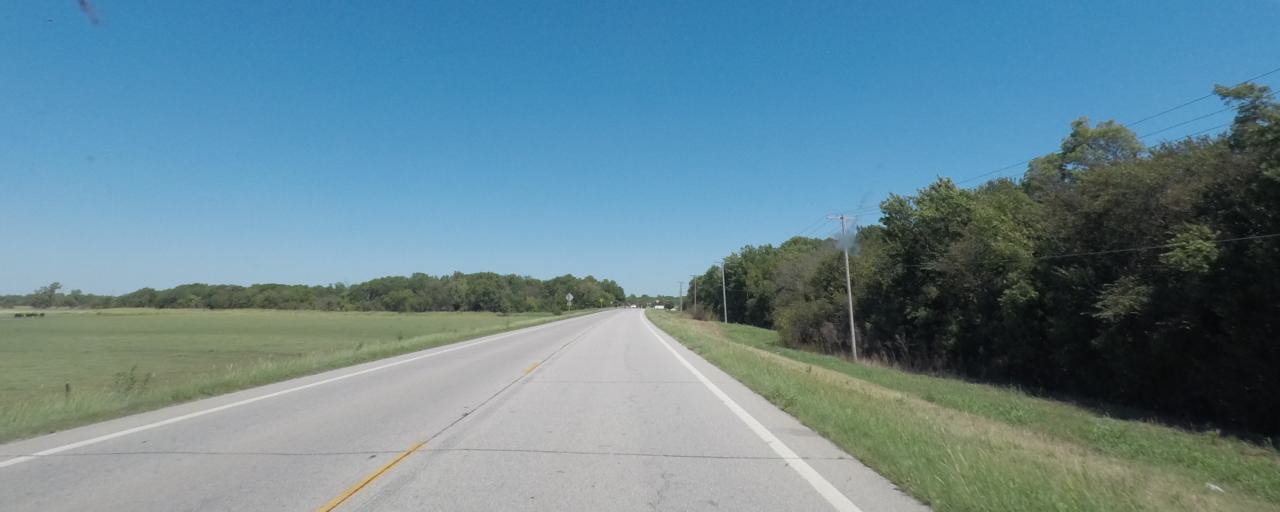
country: US
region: Kansas
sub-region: Sumner County
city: Wellington
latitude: 37.2471
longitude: -97.4033
